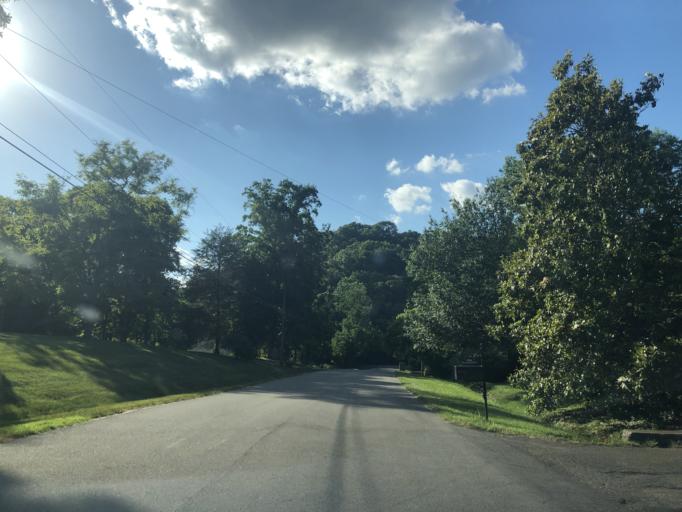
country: US
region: Tennessee
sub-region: Davidson County
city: Forest Hills
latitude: 36.0696
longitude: -86.8260
